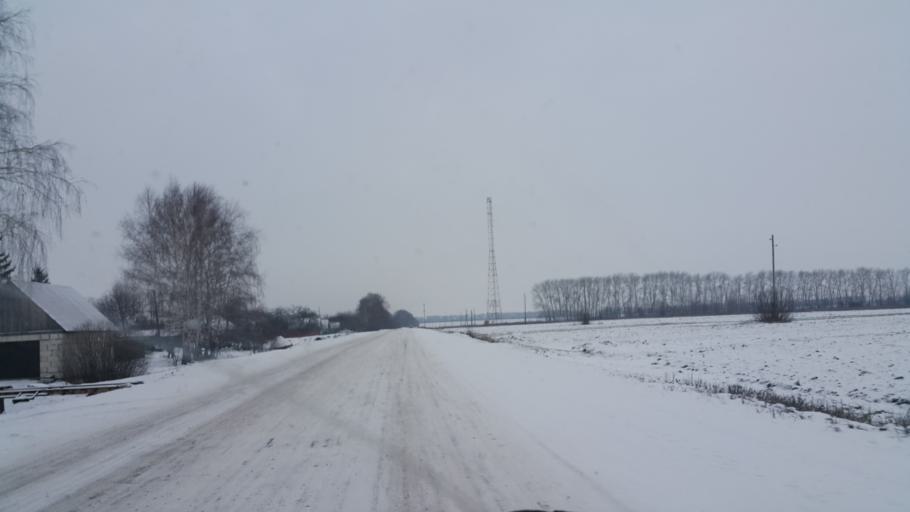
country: RU
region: Tambov
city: Inzhavino
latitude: 52.4691
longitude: 42.3875
